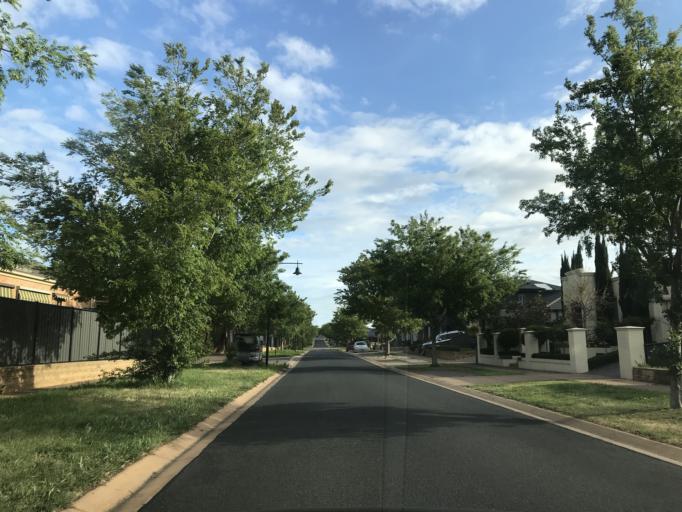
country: AU
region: Victoria
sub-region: Wyndham
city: Point Cook
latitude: -37.8927
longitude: 144.7343
